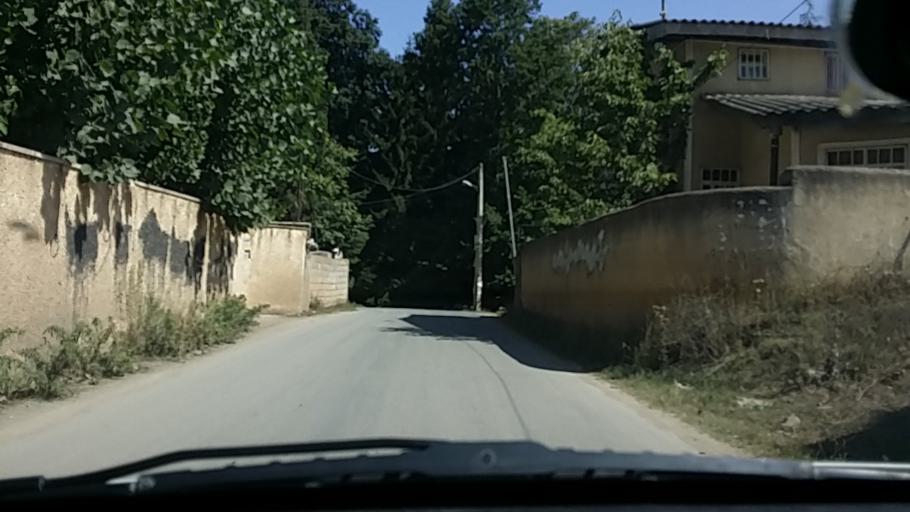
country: IR
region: Mazandaran
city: `Abbasabad
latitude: 36.5089
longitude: 51.1600
